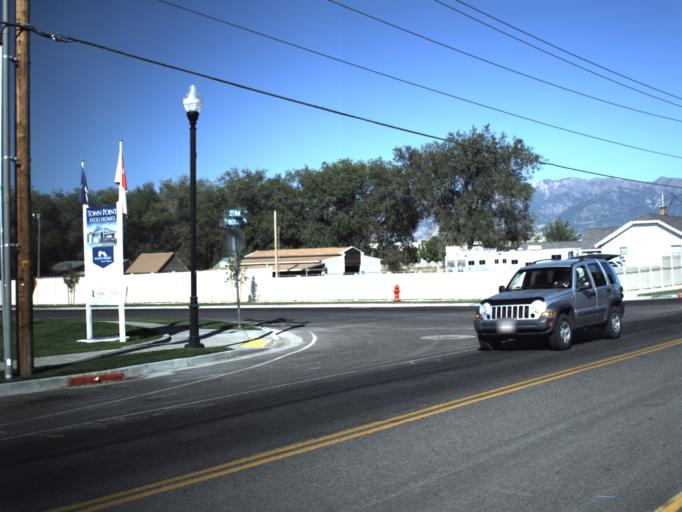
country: US
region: Utah
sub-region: Davis County
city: Clinton
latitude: 41.1398
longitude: -112.0703
